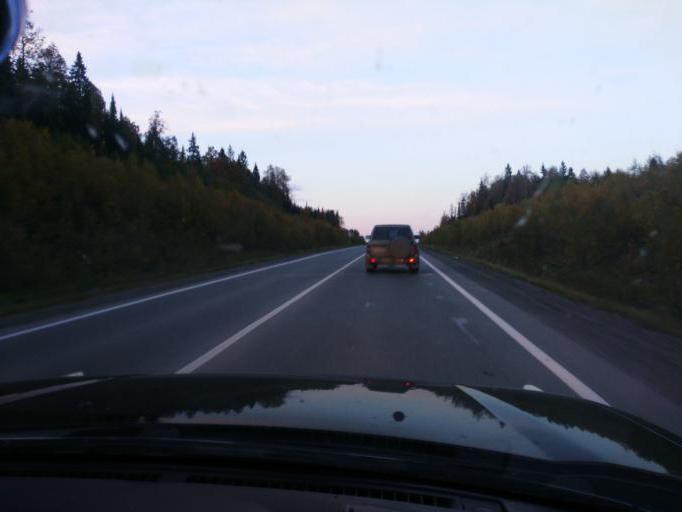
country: RU
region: Perm
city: Sylva
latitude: 58.2871
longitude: 56.7418
